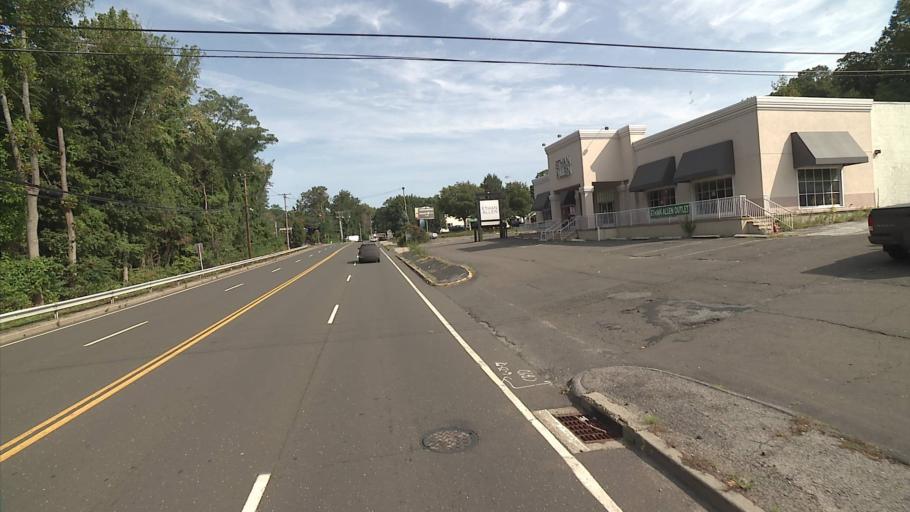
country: US
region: Connecticut
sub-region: Fairfield County
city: Norwalk
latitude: 41.1534
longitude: -73.4244
